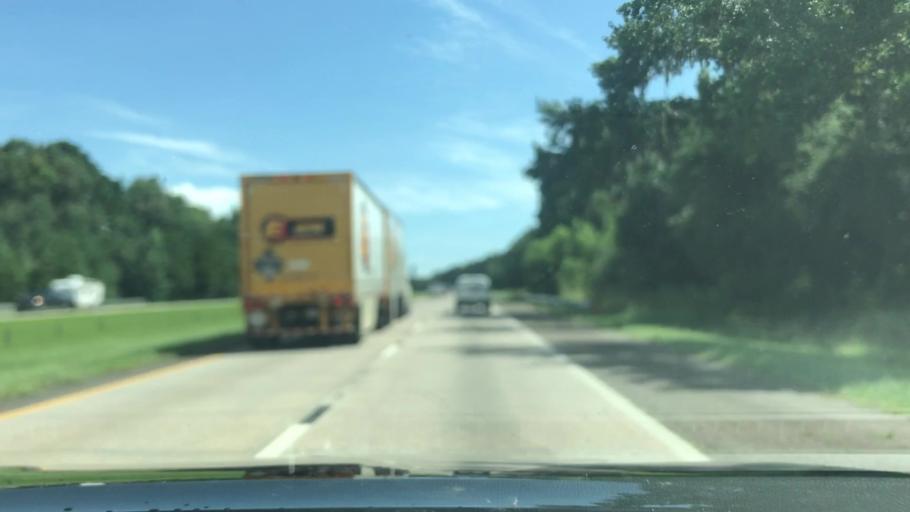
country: US
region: South Carolina
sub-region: Hampton County
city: Yemassee
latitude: 32.6555
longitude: -80.8859
